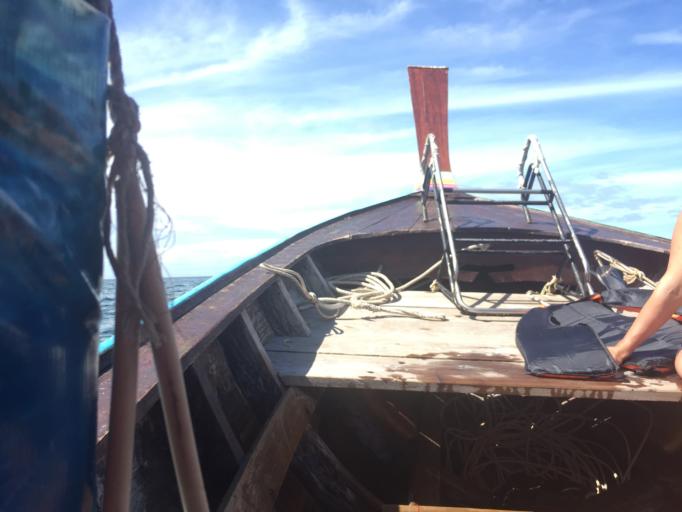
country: MY
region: Kedah
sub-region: Langkawi
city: Kuah
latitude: 6.5135
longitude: 99.2662
